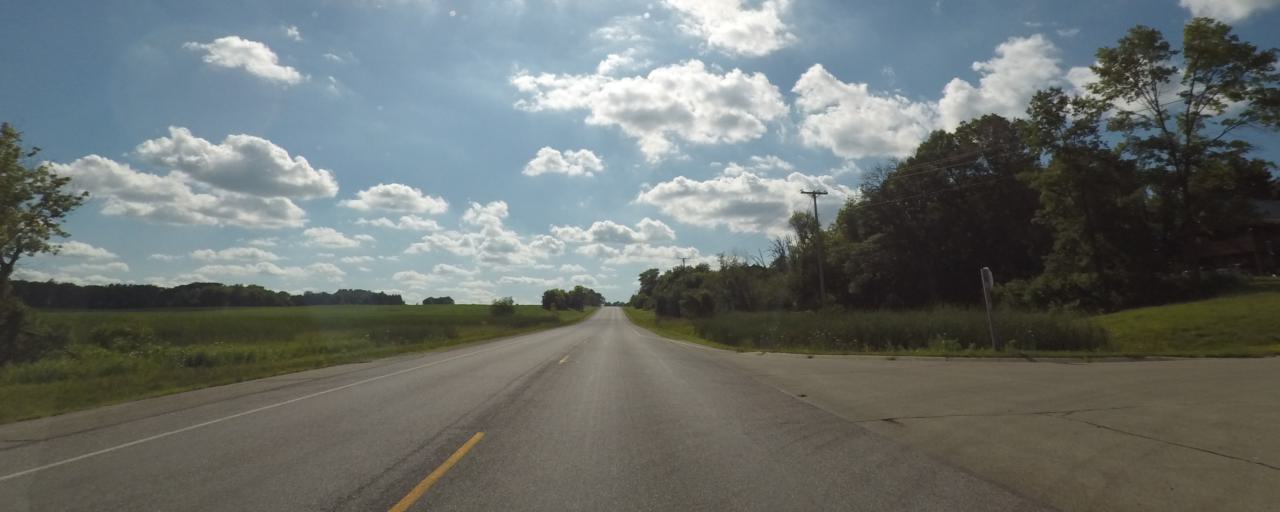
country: US
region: Wisconsin
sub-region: Dane County
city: Stoughton
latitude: 42.9198
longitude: -89.1213
